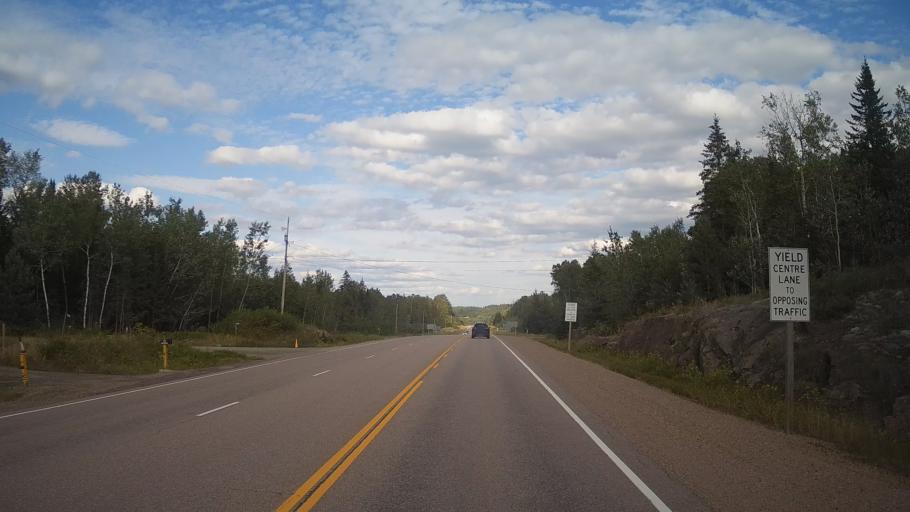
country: CA
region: Ontario
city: Mattawa
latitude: 46.2690
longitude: -78.9990
